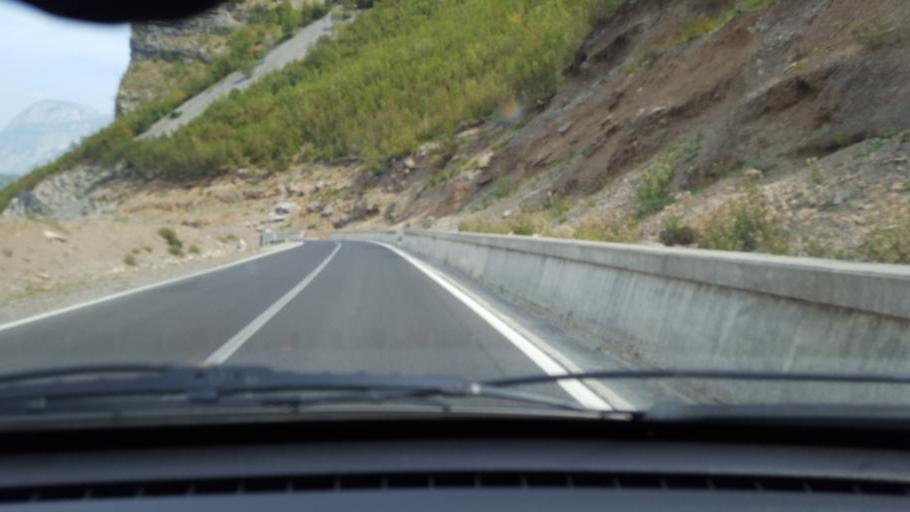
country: AL
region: Shkoder
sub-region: Rrethi i Malesia e Madhe
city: Kastrat
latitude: 42.4161
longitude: 19.4992
